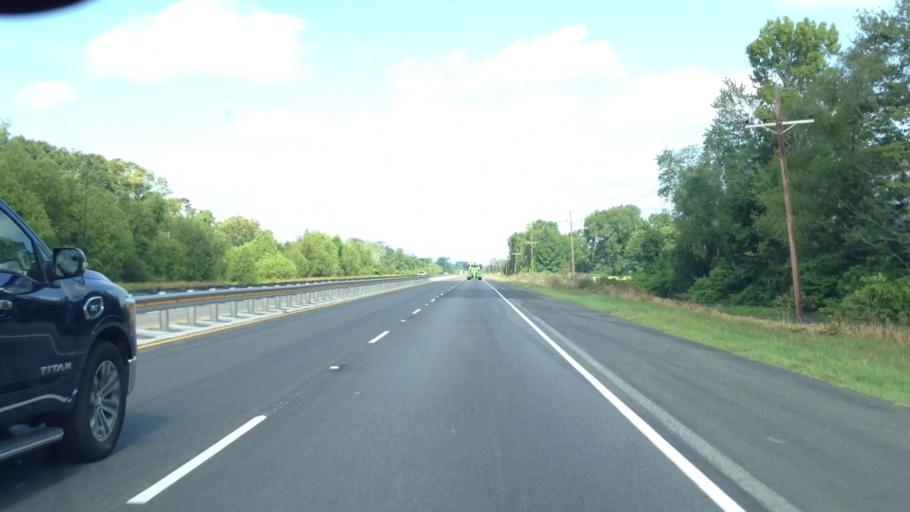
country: US
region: Louisiana
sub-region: Pointe Coupee Parish
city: Livonia
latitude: 30.5560
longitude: -91.6083
